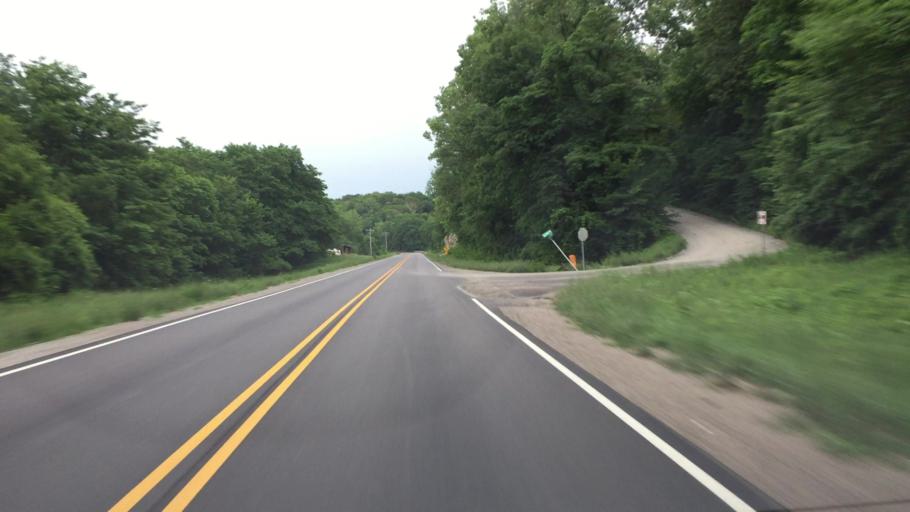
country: US
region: Iowa
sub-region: Lee County
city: Keokuk
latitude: 40.3733
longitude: -91.3882
